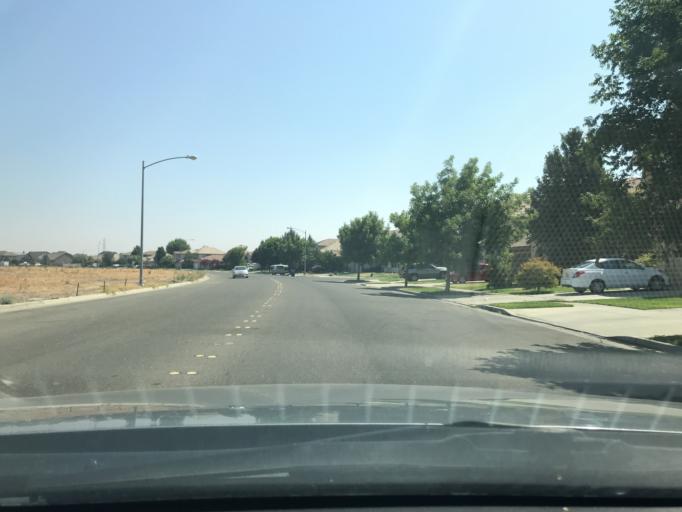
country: US
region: California
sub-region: Merced County
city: Merced
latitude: 37.3549
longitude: -120.4763
